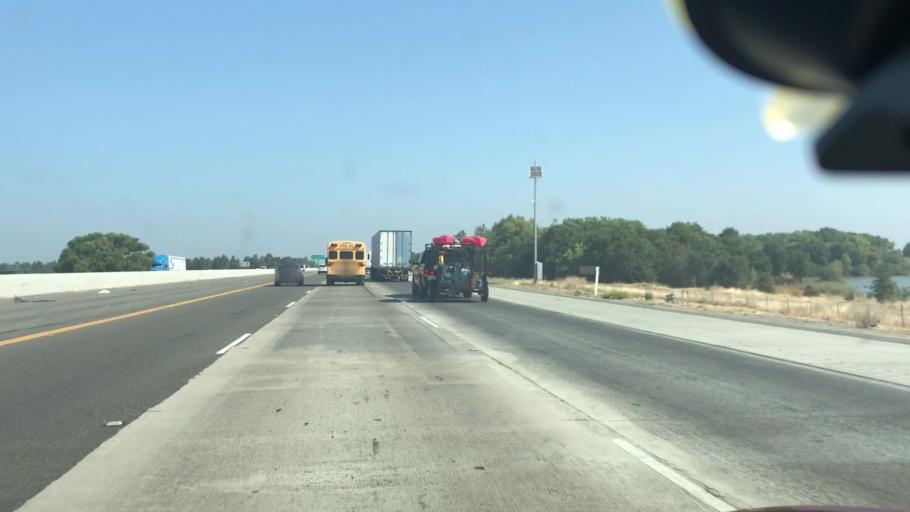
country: US
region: California
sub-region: Sacramento County
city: Parkway
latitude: 38.4426
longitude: -121.4906
